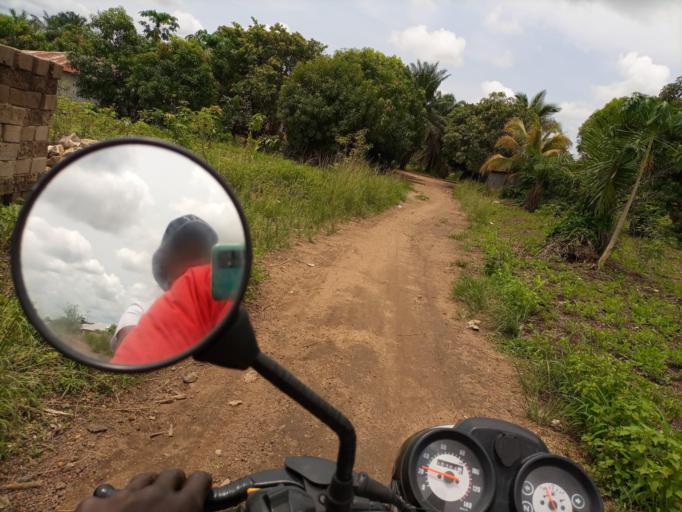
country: SL
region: Southern Province
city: Baoma
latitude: 7.9795
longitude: -11.7158
